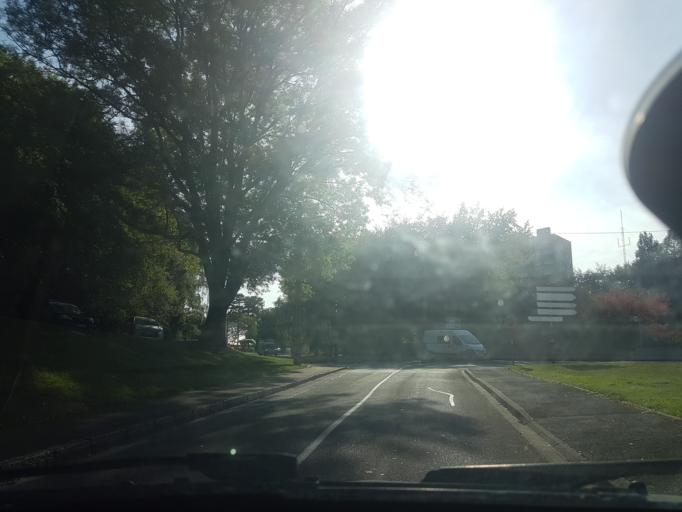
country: FR
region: Franche-Comte
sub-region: Territoire de Belfort
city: Belfort
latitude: 47.6442
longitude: 6.8633
